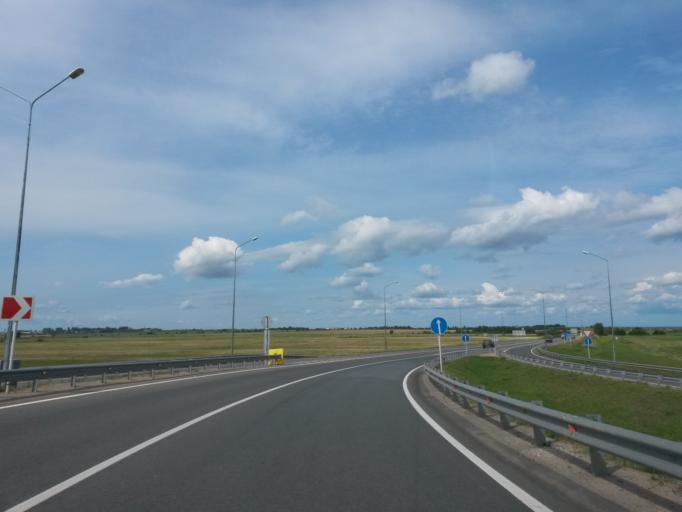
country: RU
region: Jaroslavl
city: Yaroslavl
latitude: 57.7394
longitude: 39.8931
